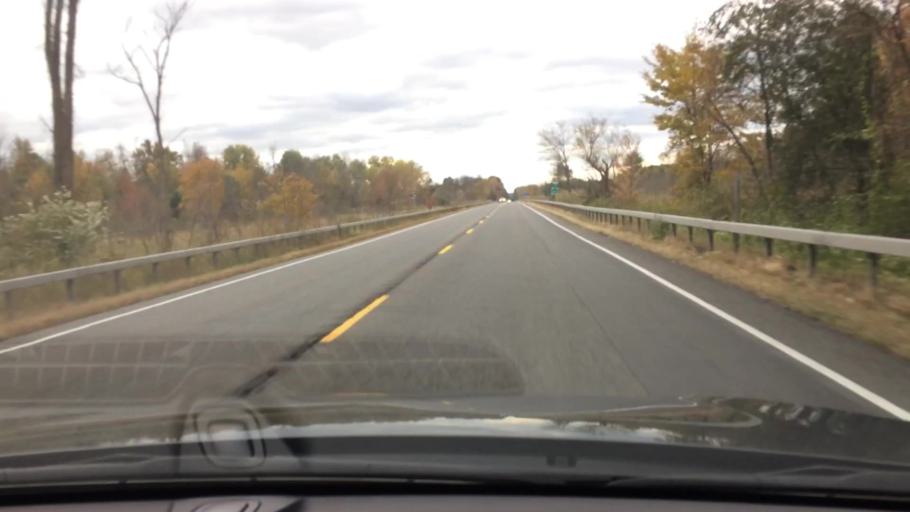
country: US
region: New York
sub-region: Columbia County
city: Kinderhook
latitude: 42.3589
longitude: -73.7053
